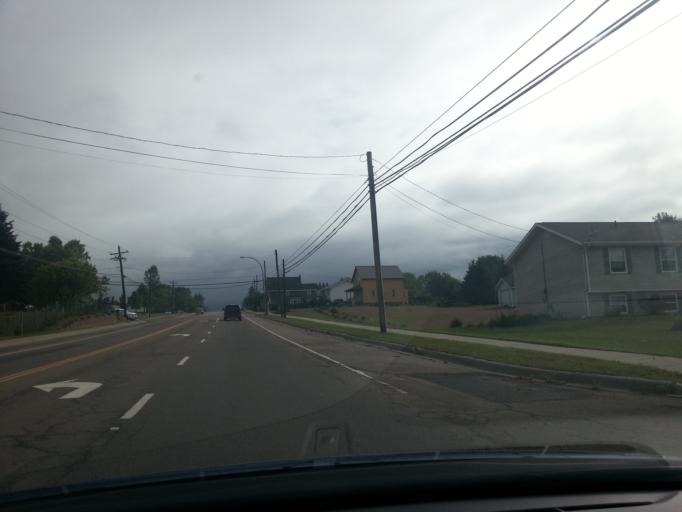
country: CA
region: Prince Edward Island
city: Charlottetown
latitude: 46.2739
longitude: -63.1075
